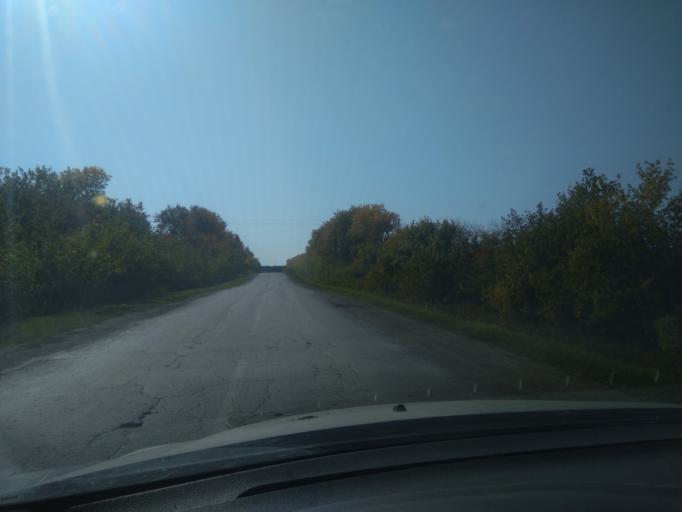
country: RU
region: Sverdlovsk
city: Pokrovskoye
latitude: 56.4623
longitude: 61.6135
